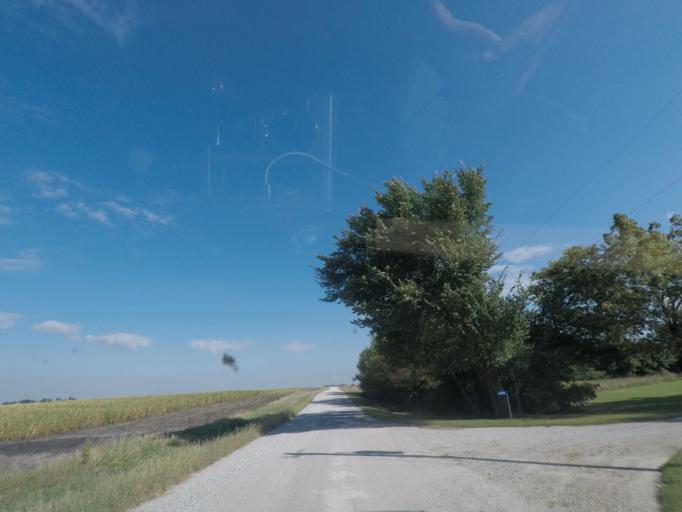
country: US
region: Iowa
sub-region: Story County
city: Nevada
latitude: 42.0362
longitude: -93.4253
